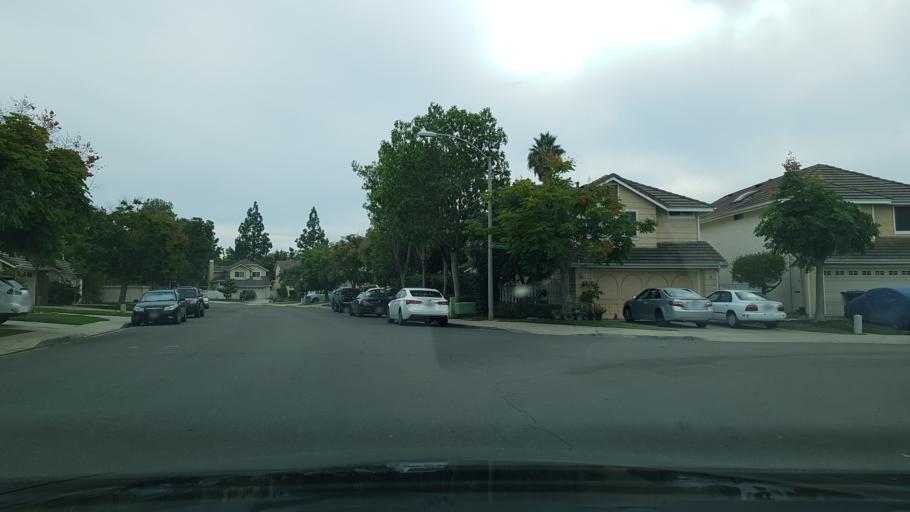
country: US
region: California
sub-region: San Diego County
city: Fairbanks Ranch
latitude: 32.9096
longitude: -117.1696
